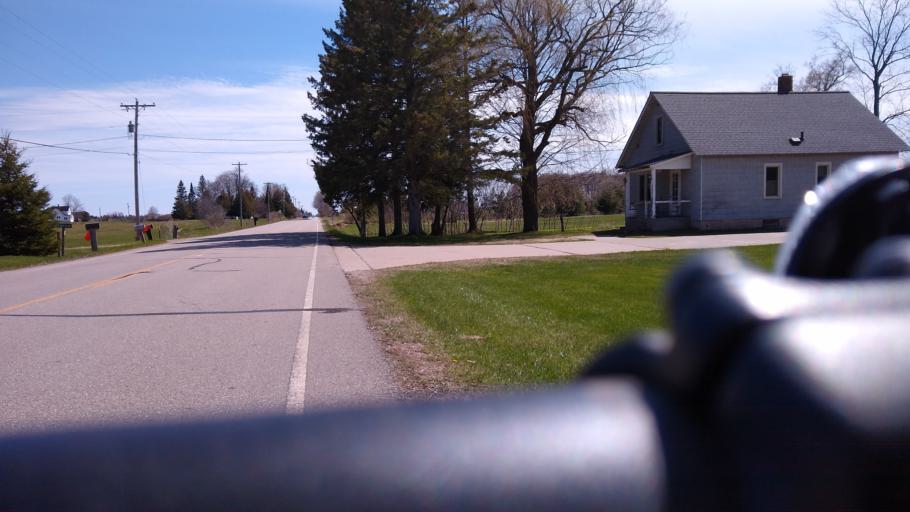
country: US
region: Michigan
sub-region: Delta County
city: Escanaba
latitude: 45.7211
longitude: -87.2025
